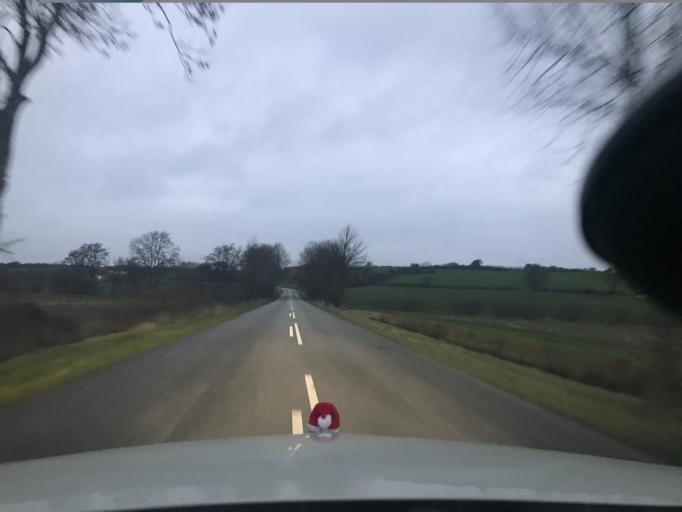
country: DK
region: South Denmark
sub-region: Sonderborg Kommune
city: Broager
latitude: 54.8692
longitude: 9.7192
